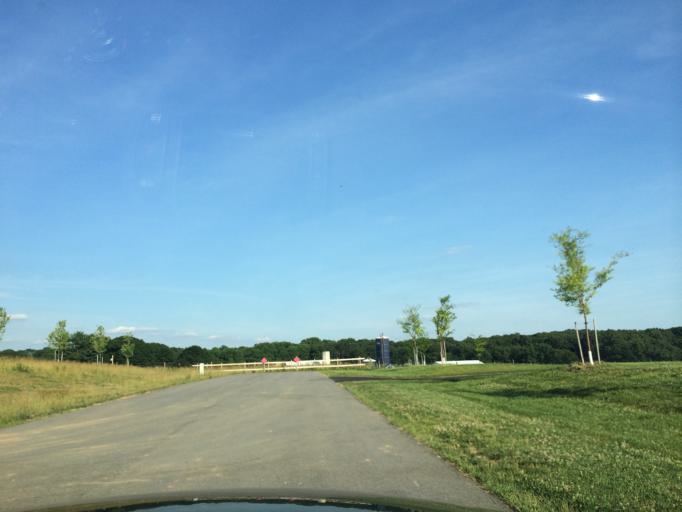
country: US
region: Maryland
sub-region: Carroll County
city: Eldersburg
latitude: 39.4177
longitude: -76.9924
